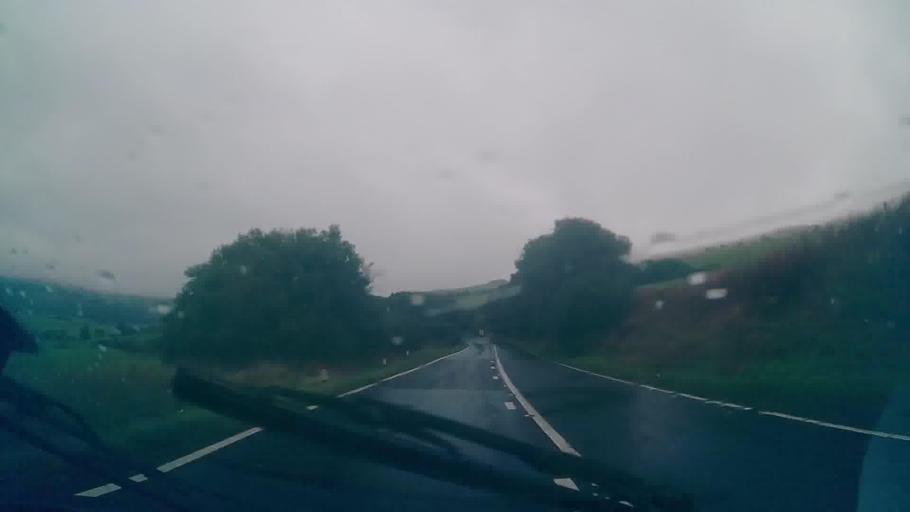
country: GB
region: Scotland
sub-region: East Ayrshire
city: New Cumnock
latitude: 55.3936
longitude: -4.1396
